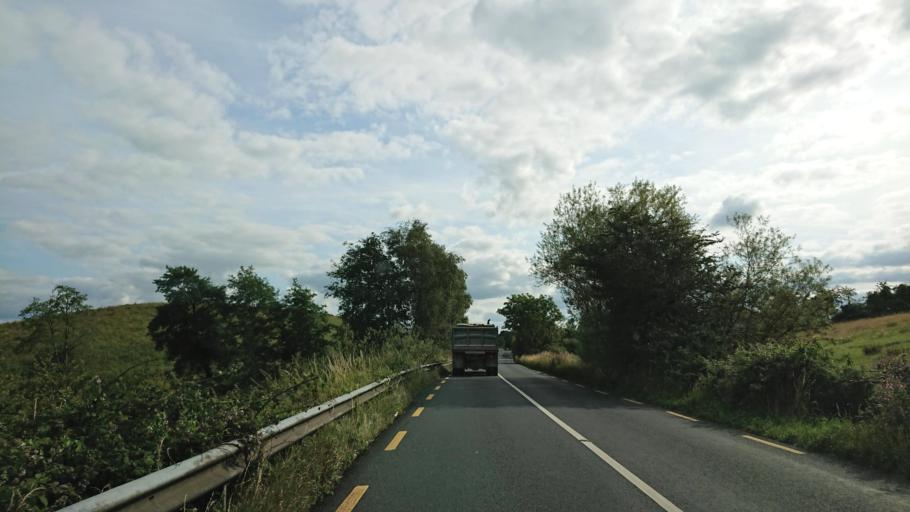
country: IE
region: Connaught
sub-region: County Leitrim
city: Carrick-on-Shannon
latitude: 53.9607
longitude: -8.0779
